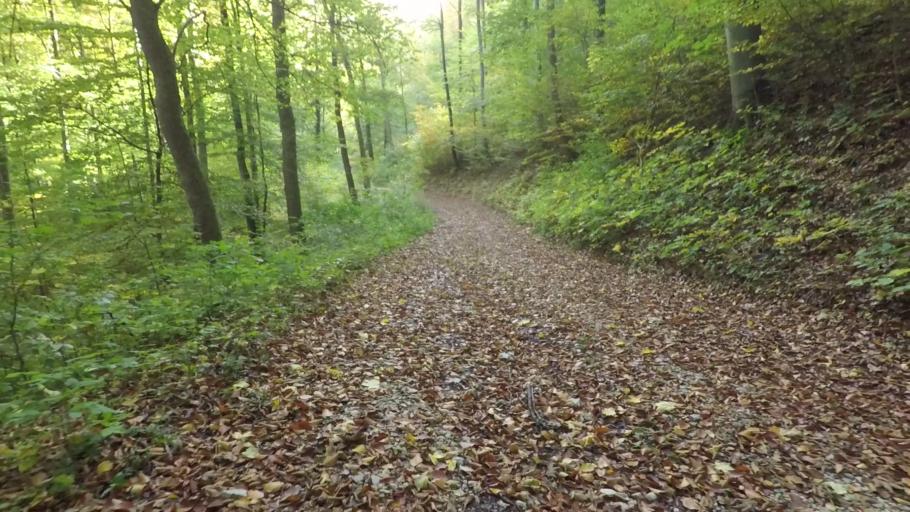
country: DE
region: Baden-Wuerttemberg
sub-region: Tuebingen Region
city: Pfullingen
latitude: 48.4412
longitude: 9.2342
